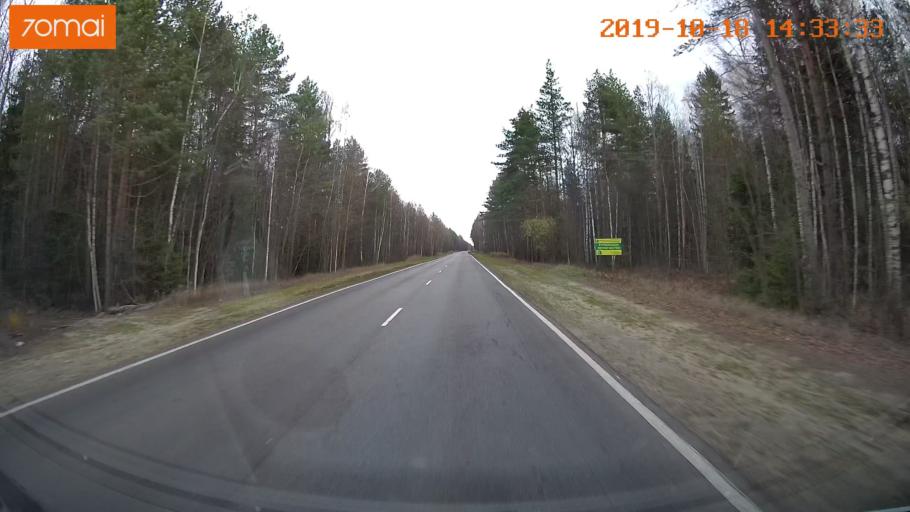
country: RU
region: Rjazan
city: Tuma
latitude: 55.2027
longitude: 40.5991
